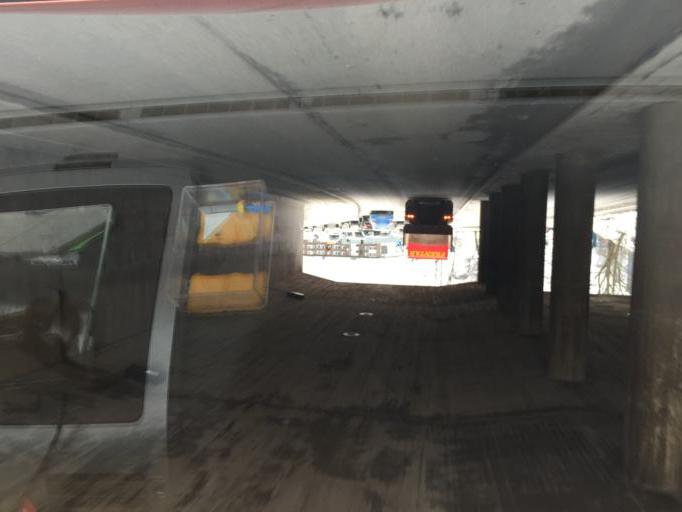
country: SE
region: Stockholm
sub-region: Stockholms Kommun
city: OEstermalm
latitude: 59.3120
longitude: 18.1095
